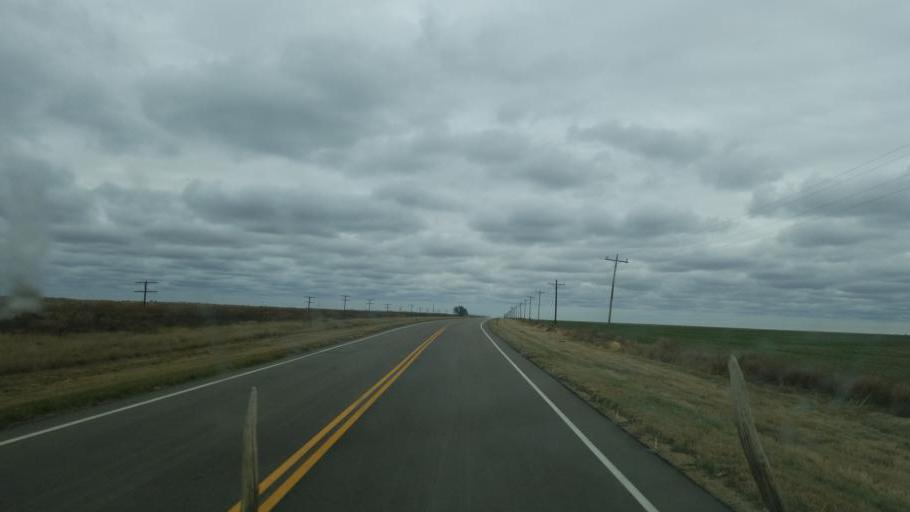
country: US
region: Colorado
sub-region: Kiowa County
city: Eads
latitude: 38.4981
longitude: -102.9773
